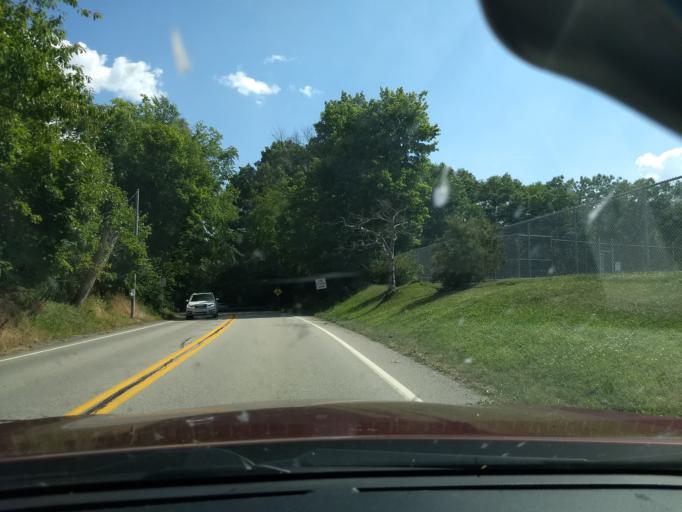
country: US
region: Pennsylvania
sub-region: Westmoreland County
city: Trafford
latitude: 40.3774
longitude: -79.7620
